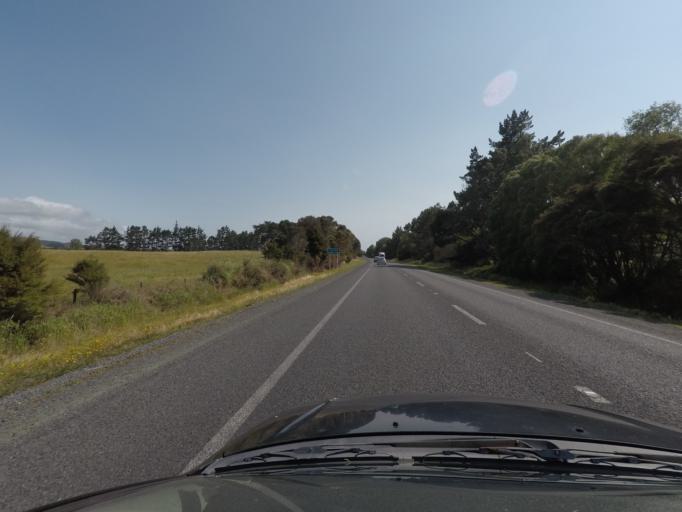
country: NZ
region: Northland
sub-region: Whangarei
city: Ruakaka
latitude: -35.9589
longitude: 174.4498
